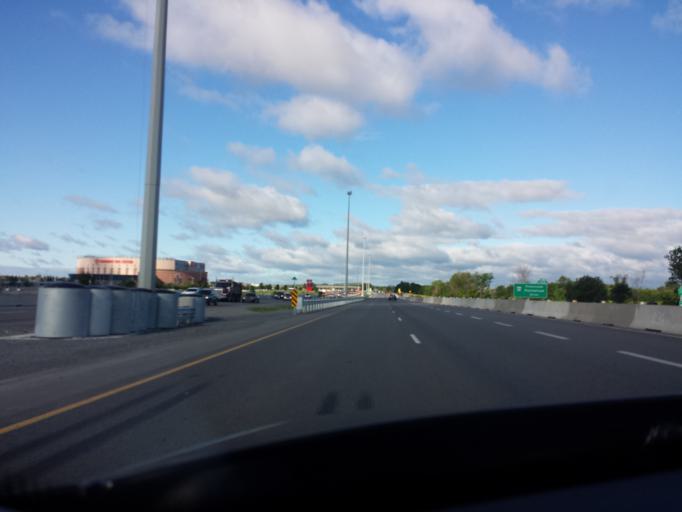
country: CA
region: Ontario
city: Bells Corners
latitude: 45.3024
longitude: -75.9202
